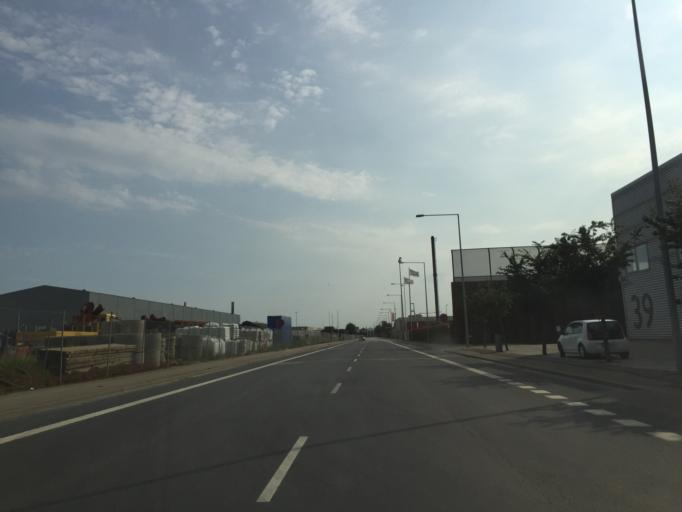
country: DK
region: Capital Region
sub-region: Gentofte Kommune
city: Charlottenlund
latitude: 55.7217
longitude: 12.6088
